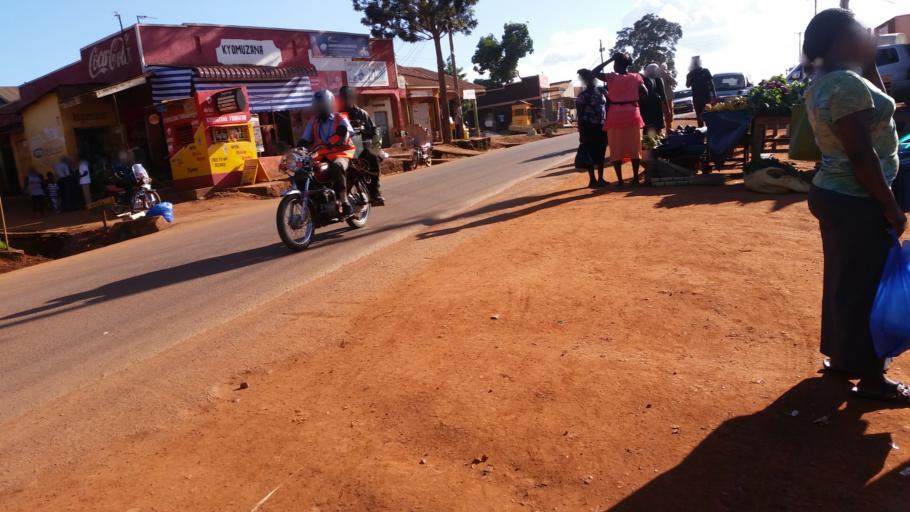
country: UG
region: Central Region
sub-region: Wakiso District
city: Kireka
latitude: 0.3220
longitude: 32.6423
